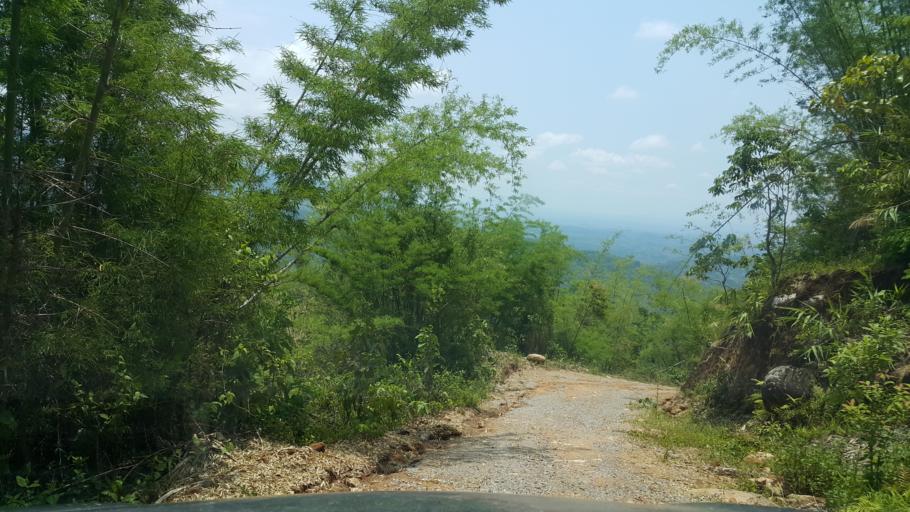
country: TH
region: Chiang Rai
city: Chiang Rai
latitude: 20.0004
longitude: 99.7080
